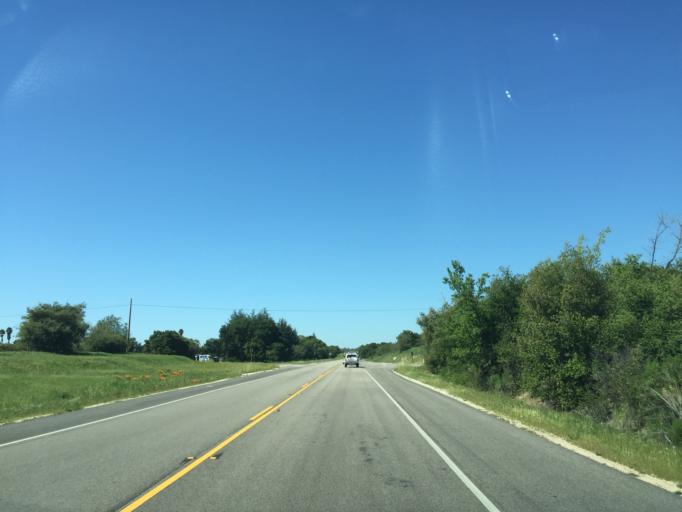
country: US
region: California
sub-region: Santa Barbara County
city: Santa Ynez
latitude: 34.6419
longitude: -120.0879
